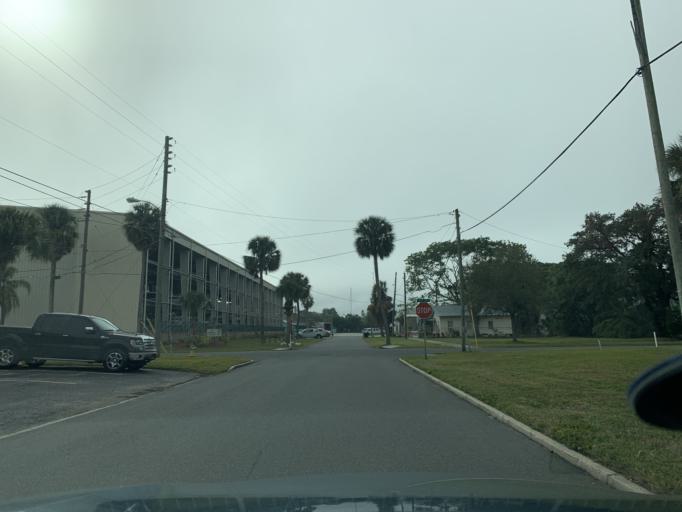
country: US
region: Florida
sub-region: Pinellas County
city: Saint Petersburg
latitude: 27.7572
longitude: -82.6354
